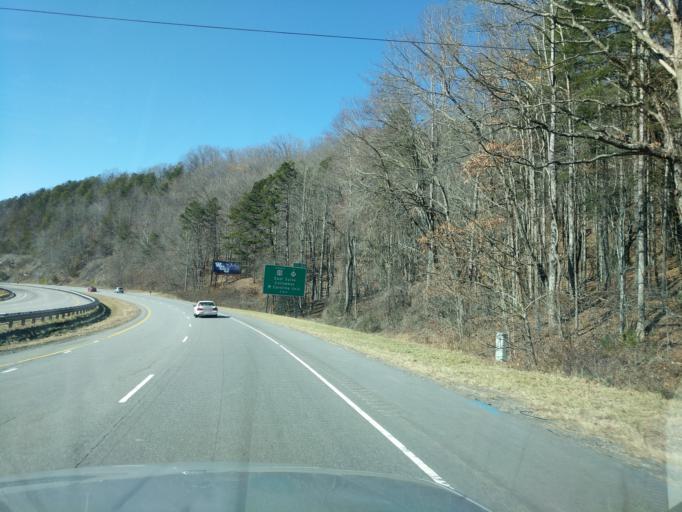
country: US
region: North Carolina
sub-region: Jackson County
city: Sylva
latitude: 35.3940
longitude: -83.1736
